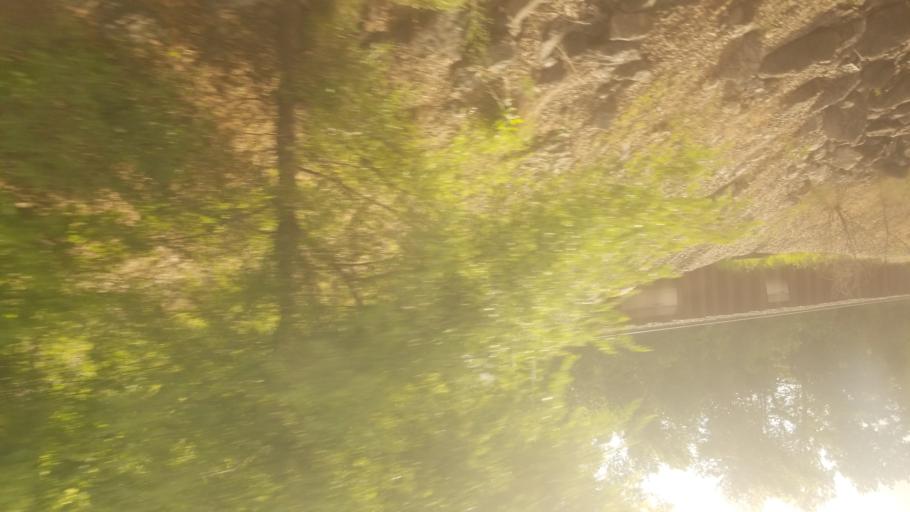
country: US
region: Kansas
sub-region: Wyandotte County
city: Edwardsville
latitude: 39.0420
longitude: -94.7974
